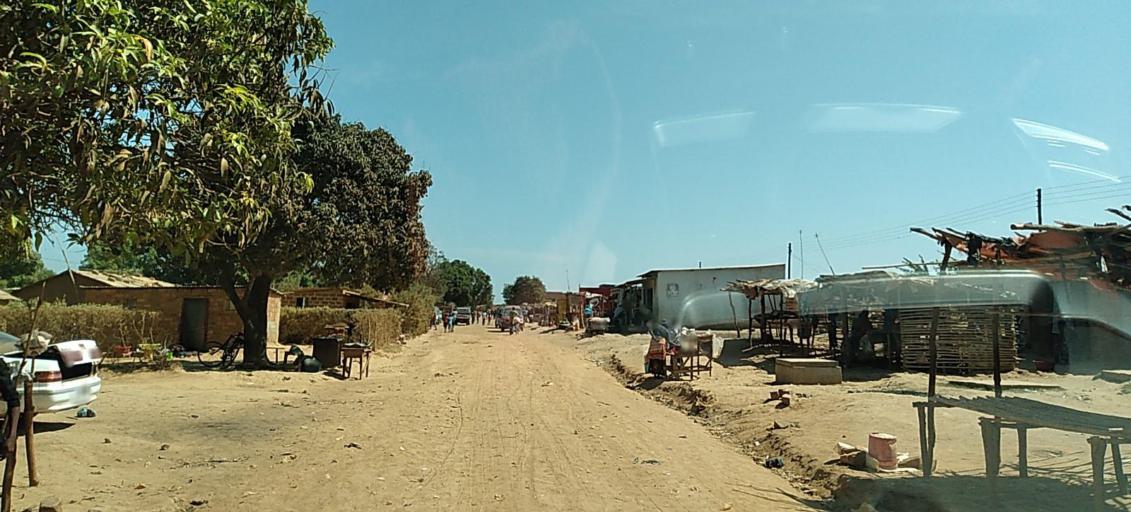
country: ZM
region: Copperbelt
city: Chililabombwe
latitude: -12.3268
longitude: 27.8603
